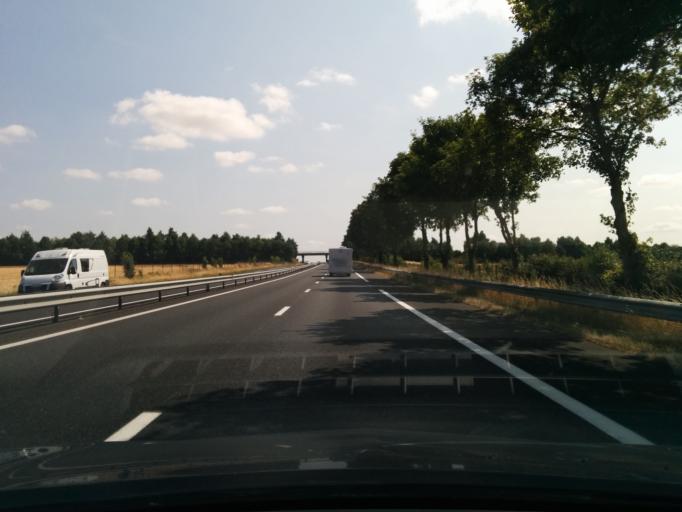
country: FR
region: Centre
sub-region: Departement de l'Indre
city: Montierchaume
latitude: 46.9673
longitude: 1.7623
